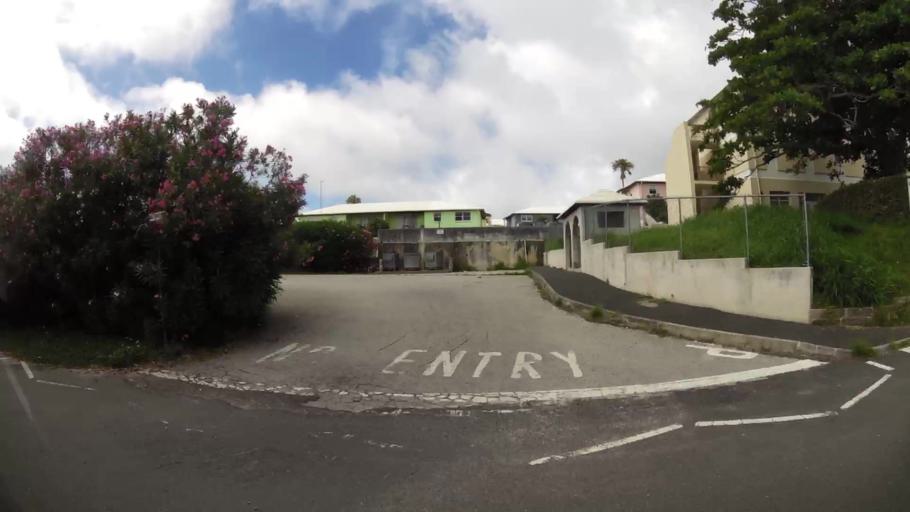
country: BM
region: Saint George
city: Saint George
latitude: 32.3837
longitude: -64.6731
